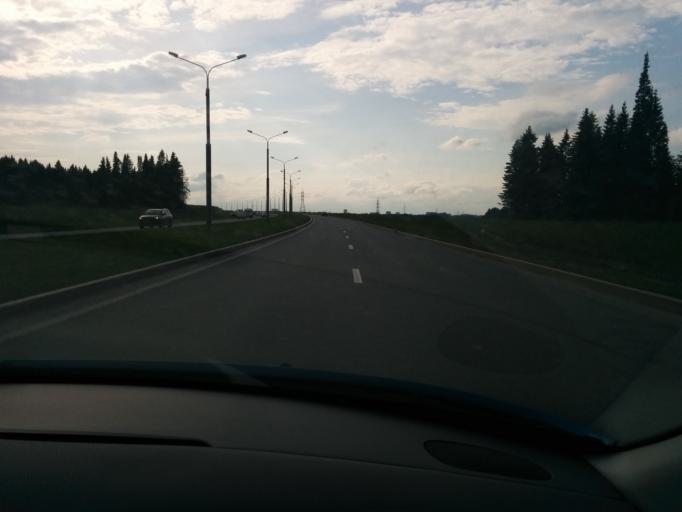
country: RU
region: Perm
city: Perm
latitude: 58.0043
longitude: 56.3695
